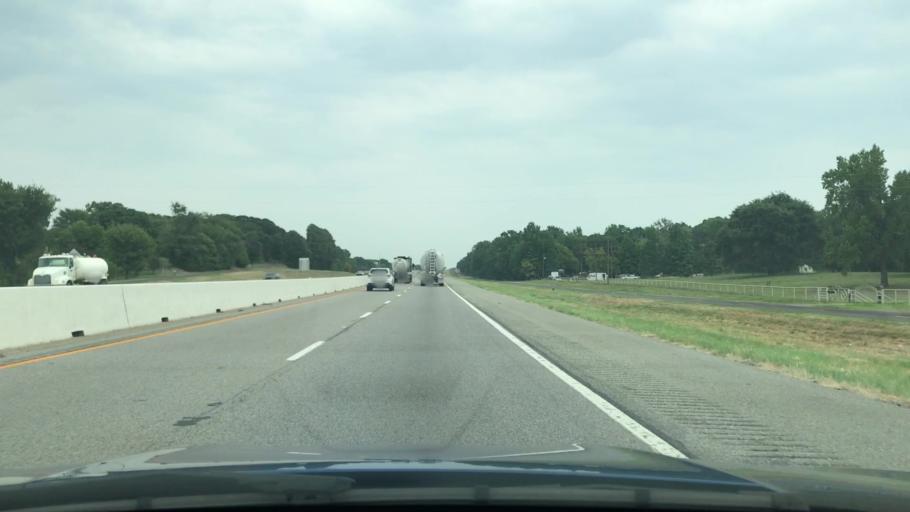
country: US
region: Texas
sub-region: Van Zandt County
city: Canton
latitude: 32.5541
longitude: -95.7910
